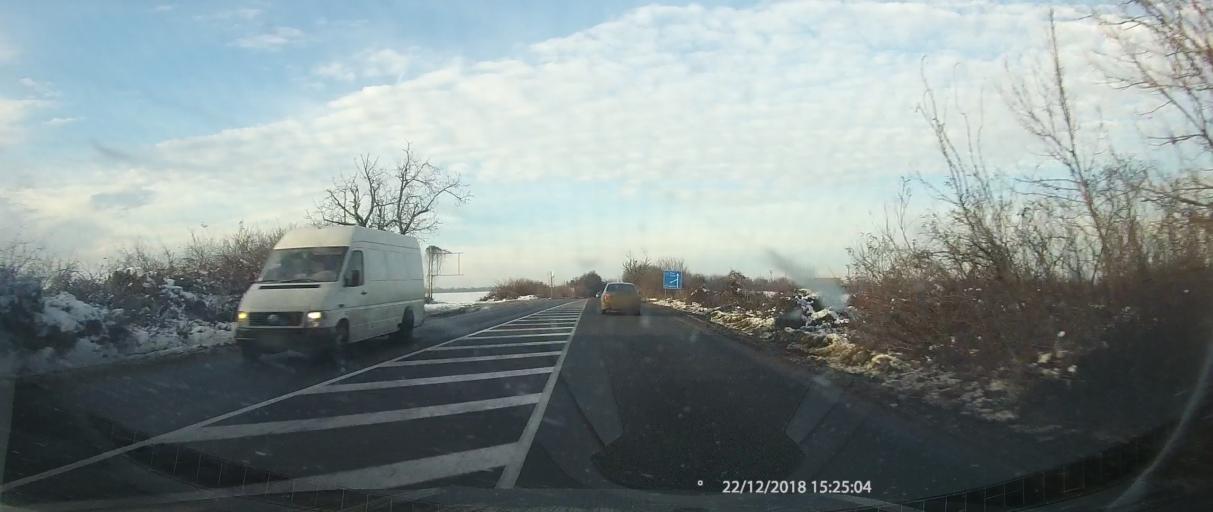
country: BG
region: Ruse
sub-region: Obshtina Ivanovo
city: Ivanovo
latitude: 43.7511
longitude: 25.9095
